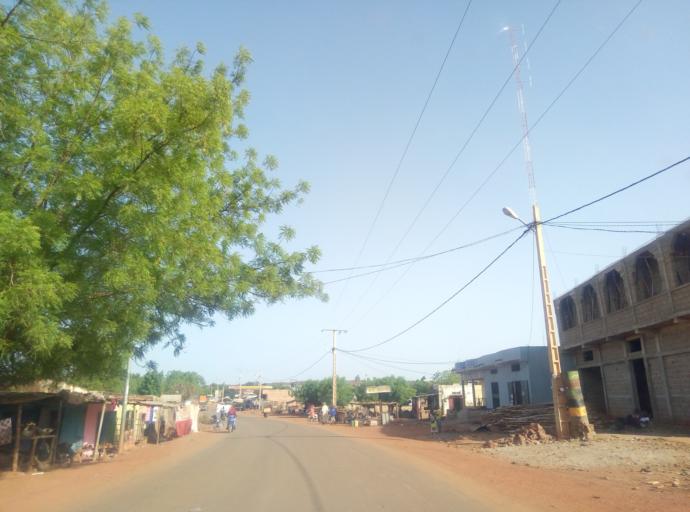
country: ML
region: Bamako
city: Bamako
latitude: 12.6130
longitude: -7.7768
